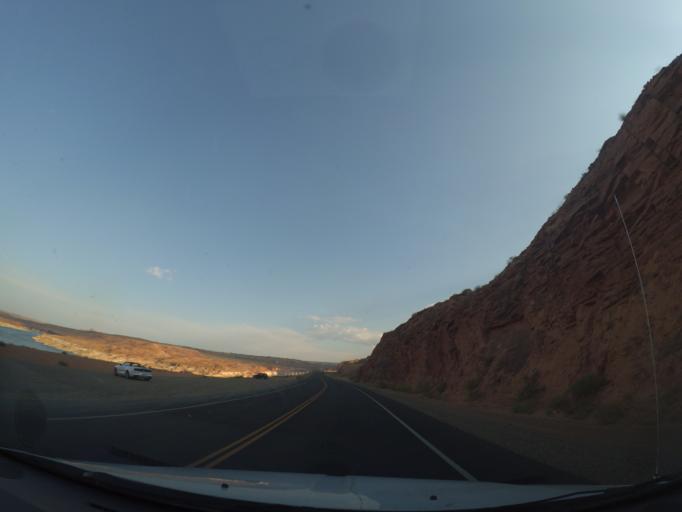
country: US
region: Arizona
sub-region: Coconino County
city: Page
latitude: 36.9576
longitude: -111.4939
